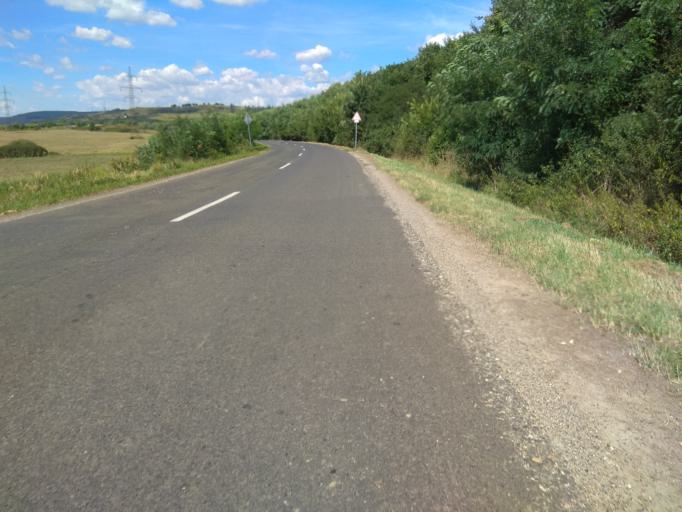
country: HU
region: Borsod-Abauj-Zemplen
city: Sajokaza
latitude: 48.2860
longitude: 20.6193
